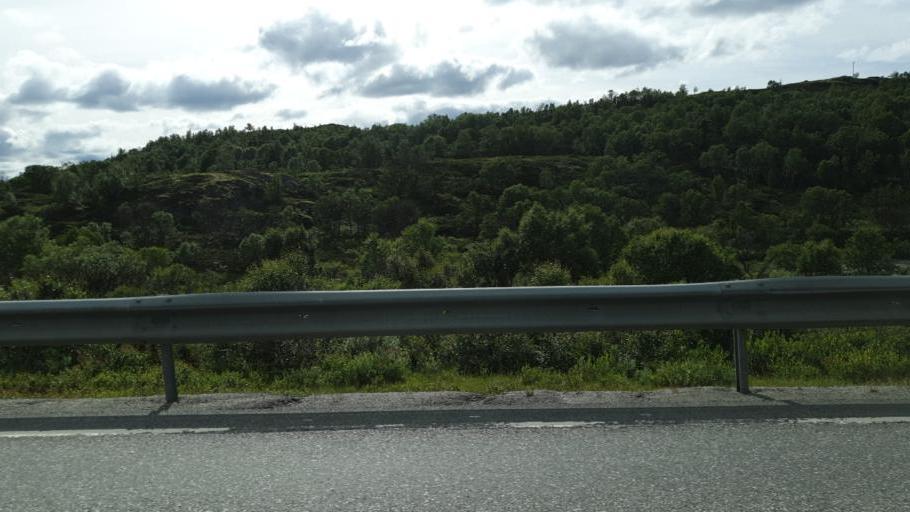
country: NO
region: Sor-Trondelag
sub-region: Oppdal
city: Oppdal
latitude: 62.2865
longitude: 9.5994
